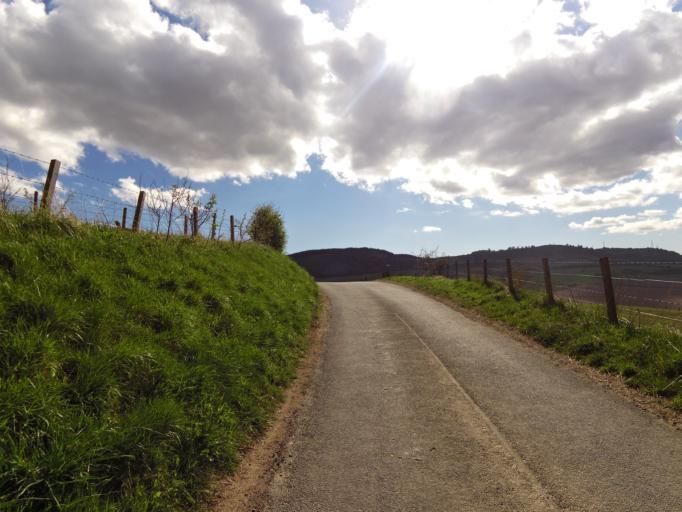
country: GB
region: Scotland
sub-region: Fife
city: Newburgh
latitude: 56.3428
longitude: -3.2529
